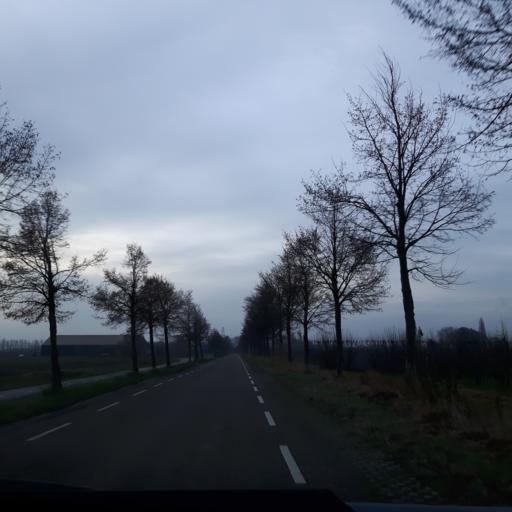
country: NL
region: Zeeland
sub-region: Gemeente Terneuzen
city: Terneuzen
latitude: 51.4181
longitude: 3.8554
